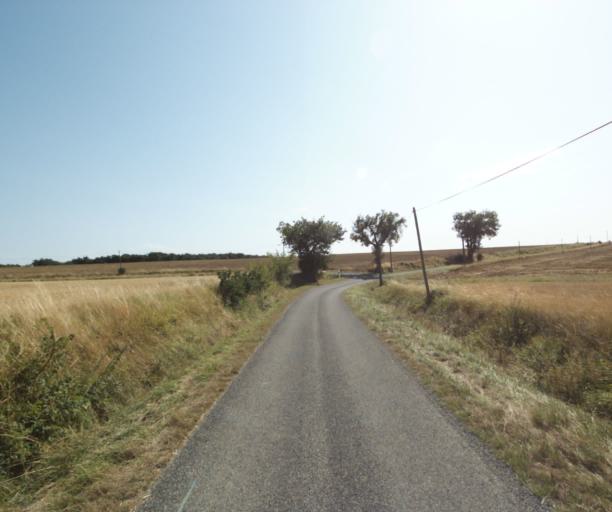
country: FR
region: Midi-Pyrenees
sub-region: Departement de la Haute-Garonne
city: Saint-Felix-Lauragais
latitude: 43.4260
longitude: 1.8447
